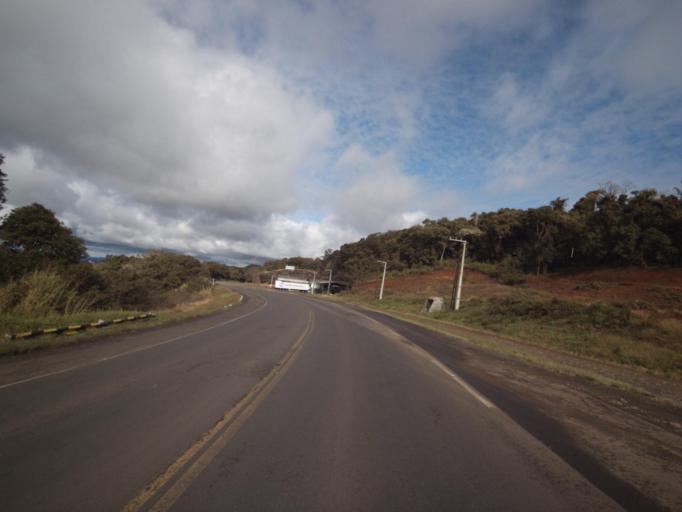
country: BR
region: Santa Catarina
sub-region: Concordia
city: Concordia
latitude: -27.2035
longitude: -51.9487
